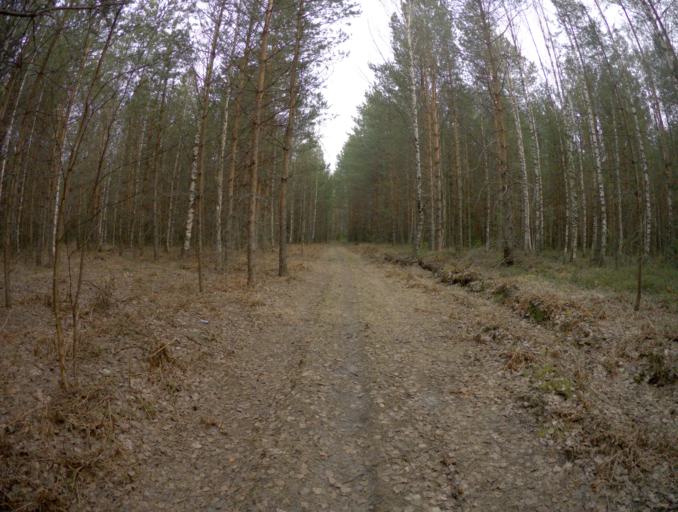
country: RU
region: Vladimir
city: Raduzhnyy
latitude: 55.9315
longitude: 40.2594
